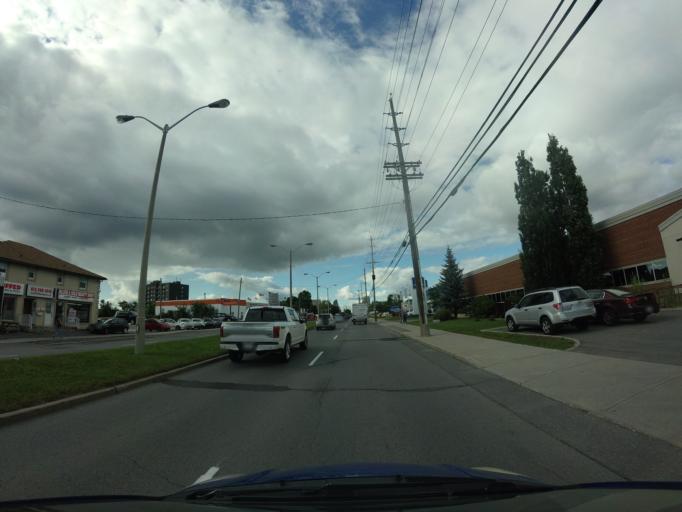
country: CA
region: Ontario
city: Ottawa
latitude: 45.4311
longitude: -75.6411
